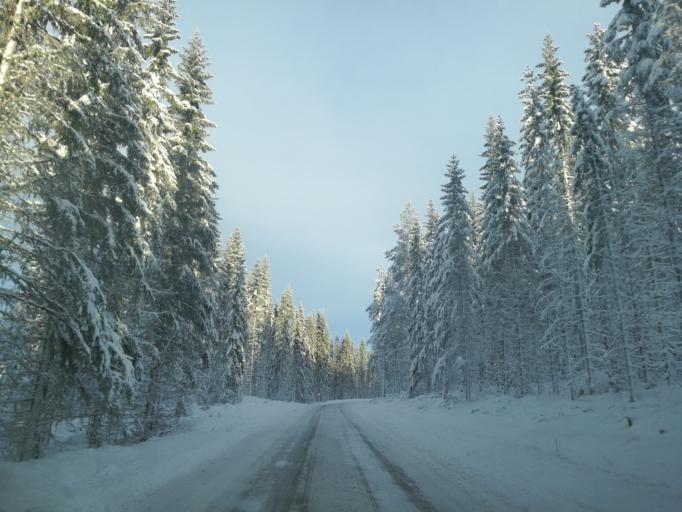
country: SE
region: Vaermland
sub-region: Torsby Kommun
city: Torsby
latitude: 60.6539
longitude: 12.8022
